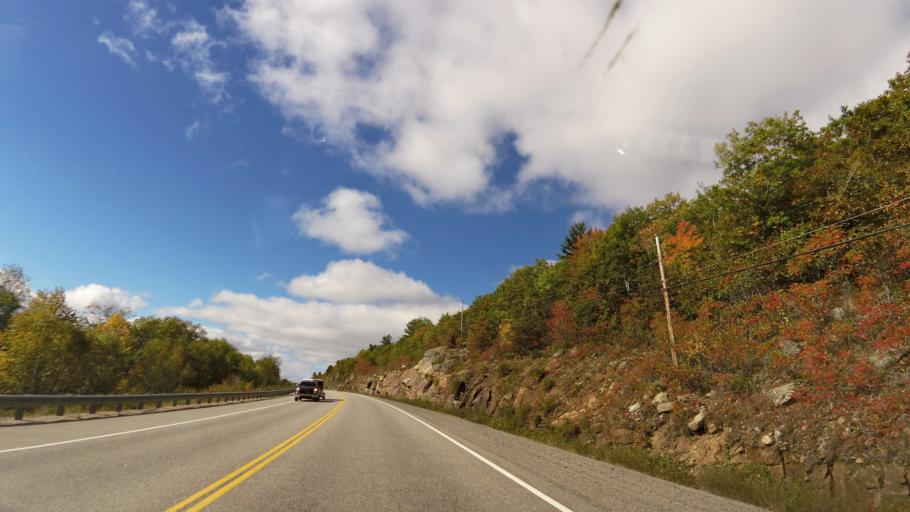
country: CA
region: Ontario
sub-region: Nipissing District
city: North Bay
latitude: 46.3537
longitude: -79.6235
